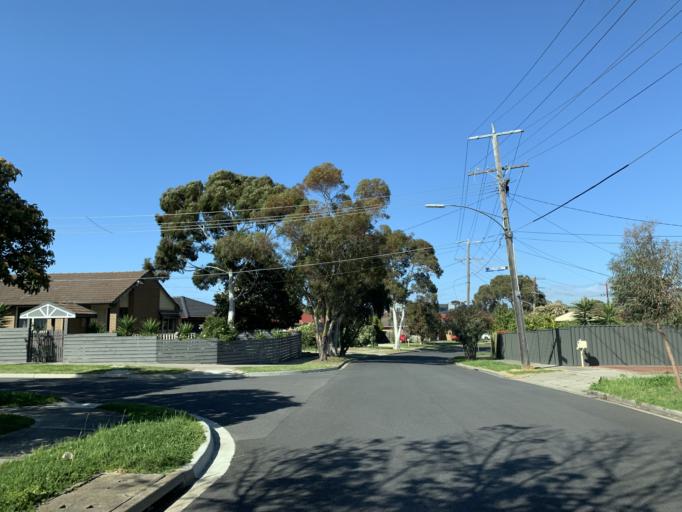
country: AU
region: Victoria
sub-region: Brimbank
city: Kealba
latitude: -37.7376
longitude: 144.8260
